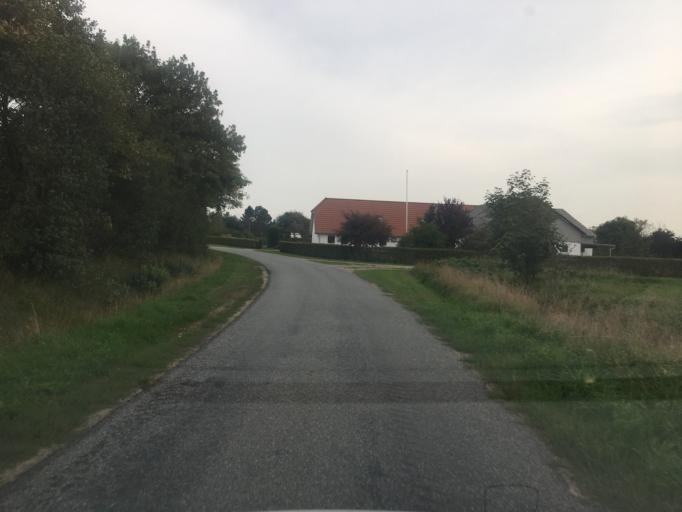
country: DK
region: South Denmark
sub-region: Tonder Kommune
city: Logumkloster
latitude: 55.0402
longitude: 8.9050
